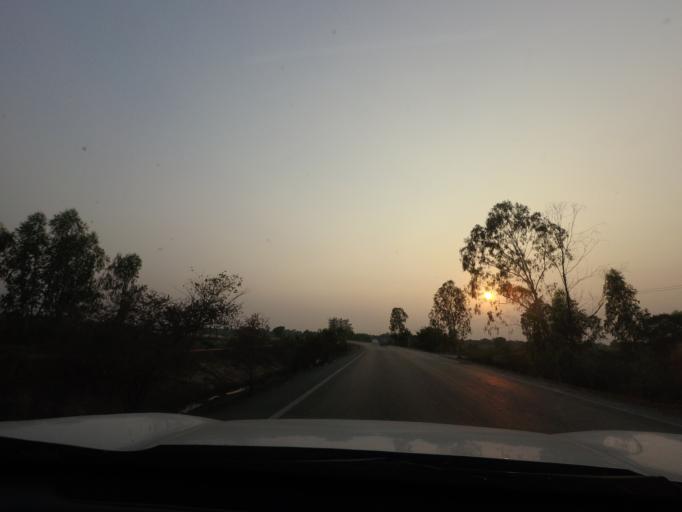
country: TH
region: Nakhon Nayok
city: Ongkharak
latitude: 14.1483
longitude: 101.0343
